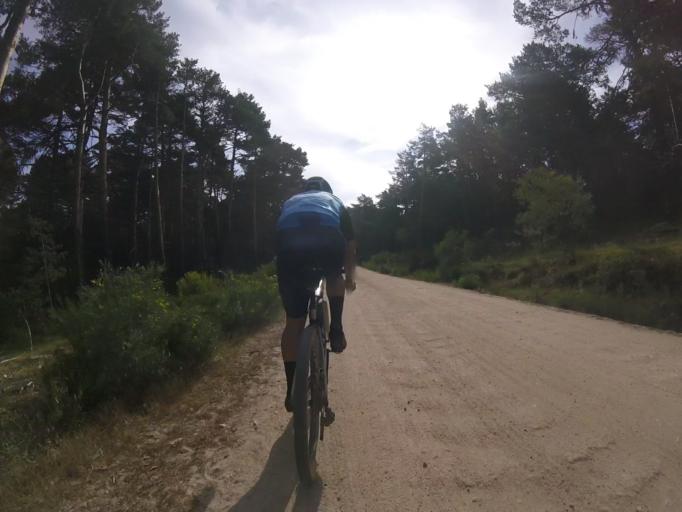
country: ES
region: Castille and Leon
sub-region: Provincia de Avila
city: Peguerinos
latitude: 40.6427
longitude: -4.1805
